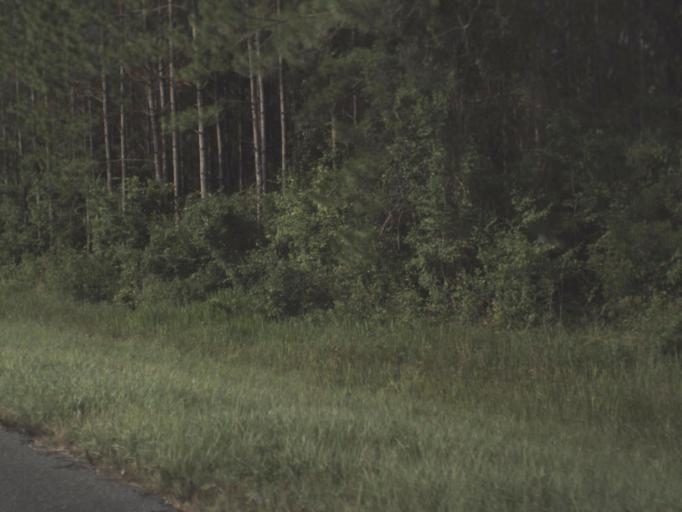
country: US
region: Florida
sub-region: Taylor County
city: Perry
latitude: 30.2098
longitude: -83.6106
